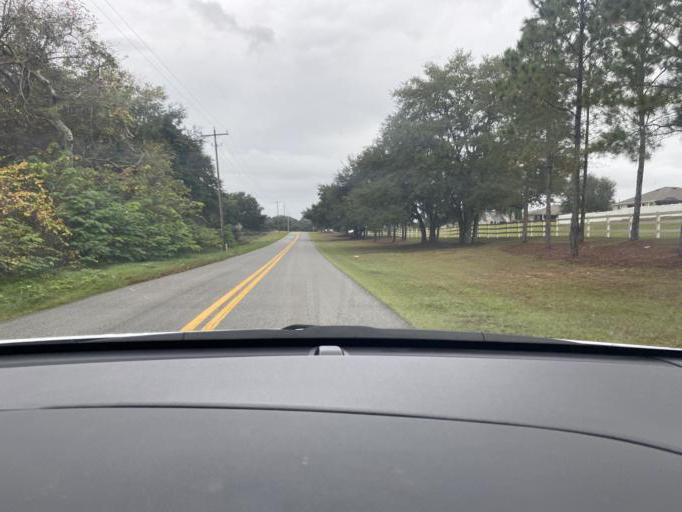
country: US
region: Florida
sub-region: Lake County
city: Clermont
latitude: 28.5969
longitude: -81.7983
